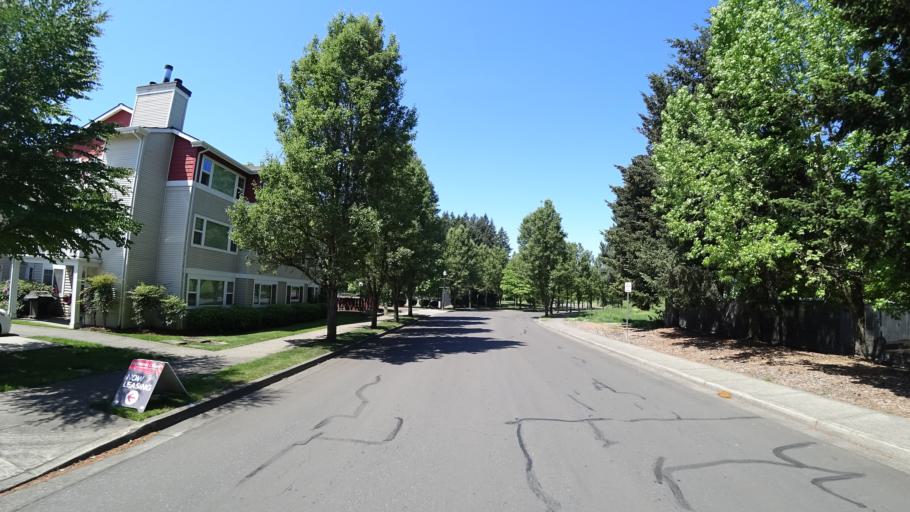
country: US
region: Oregon
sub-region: Washington County
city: Rockcreek
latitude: 45.5242
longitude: -122.9270
